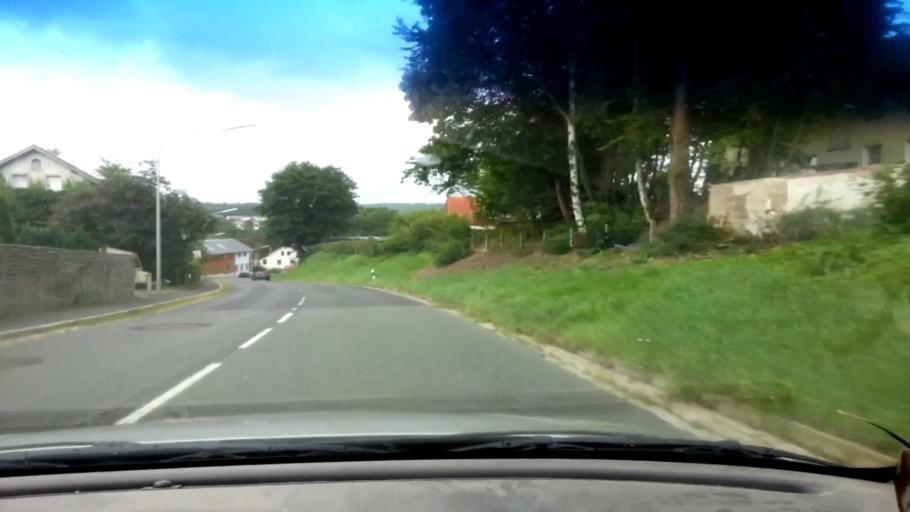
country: DE
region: Bavaria
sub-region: Upper Franconia
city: Schirnding
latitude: 50.0832
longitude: 12.2254
